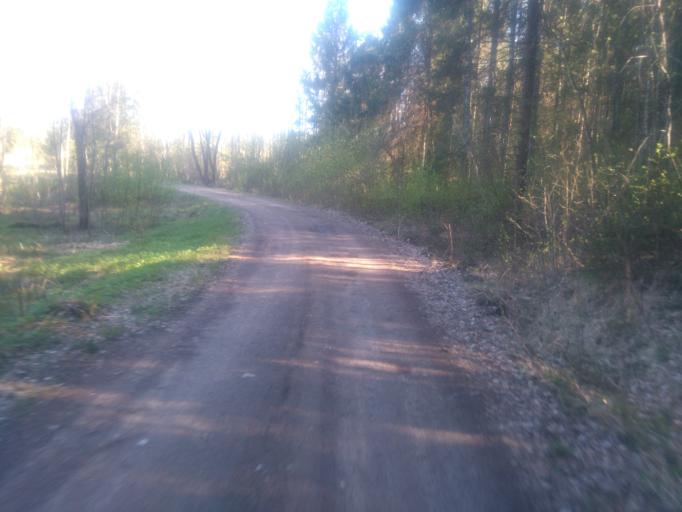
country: LV
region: Vecpiebalga
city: Vecpiebalga
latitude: 57.0077
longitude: 25.8437
